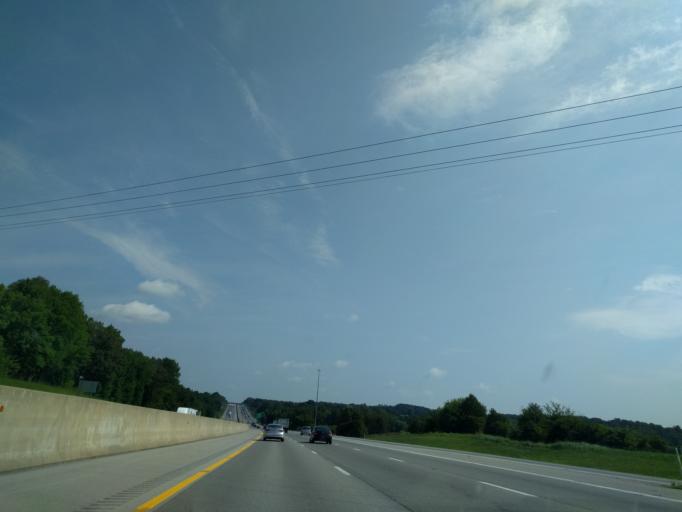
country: US
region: Kentucky
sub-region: Simpson County
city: Franklin
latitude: 36.6899
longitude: -86.5361
